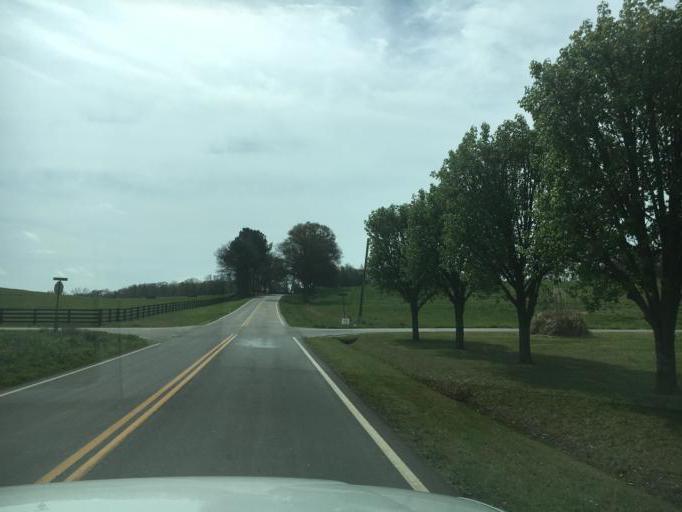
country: US
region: Georgia
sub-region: Franklin County
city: Lavonia
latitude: 34.3875
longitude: -83.0593
